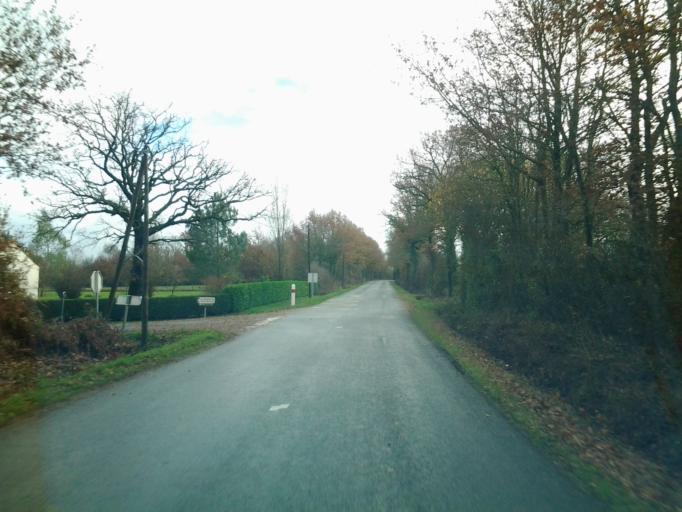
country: FR
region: Pays de la Loire
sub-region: Departement de la Vendee
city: Saint-Florent-des-Bois
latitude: 46.6351
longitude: -1.3380
